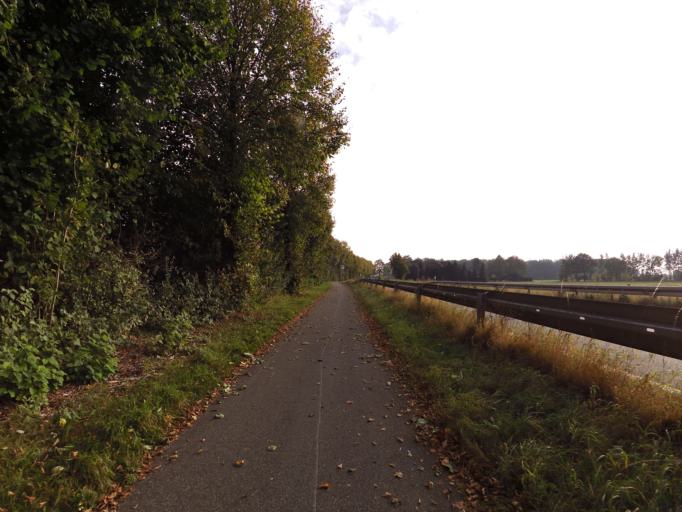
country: DE
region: North Rhine-Westphalia
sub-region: Regierungsbezirk Dusseldorf
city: Bocholt
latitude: 51.8068
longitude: 6.5622
